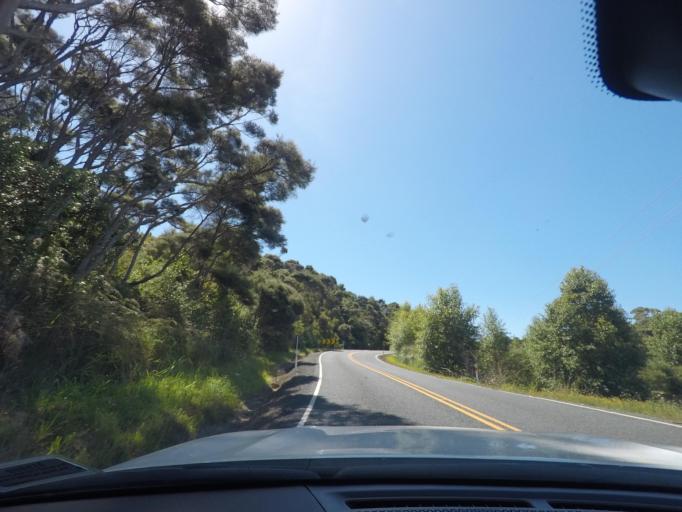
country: NZ
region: Auckland
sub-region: Auckland
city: Parakai
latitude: -36.5796
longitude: 174.3266
